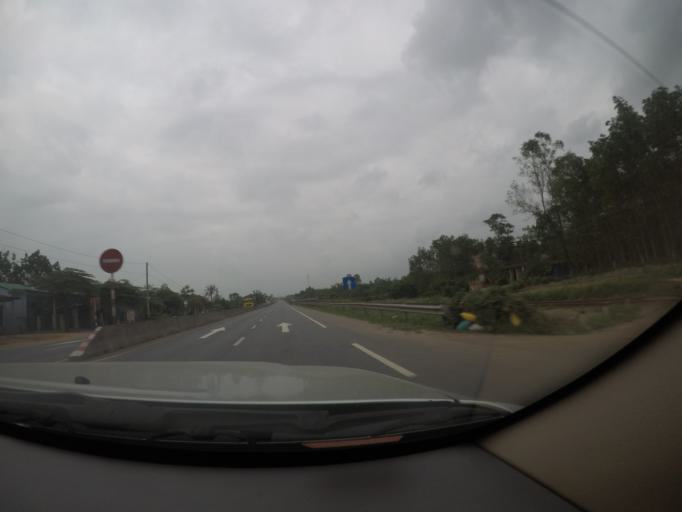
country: VN
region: Quang Tri
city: Hai Lang
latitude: 16.6416
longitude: 107.2942
